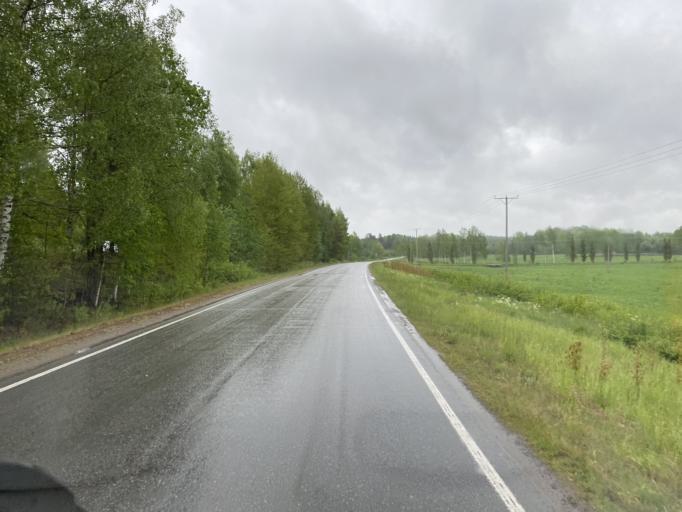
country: FI
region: Pirkanmaa
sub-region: Etelae-Pirkanmaa
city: Urjala
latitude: 61.0427
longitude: 23.4258
